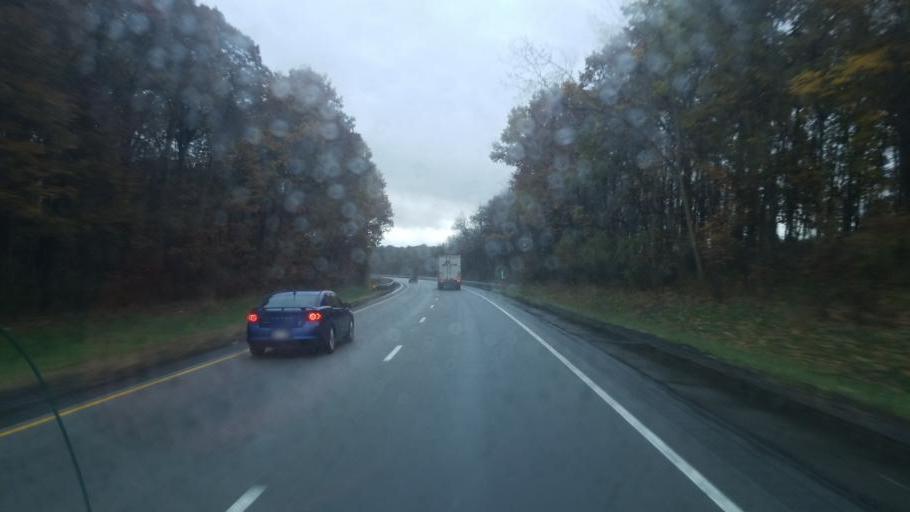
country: US
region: Pennsylvania
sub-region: Clarion County
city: Clarion
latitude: 41.1740
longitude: -79.2922
